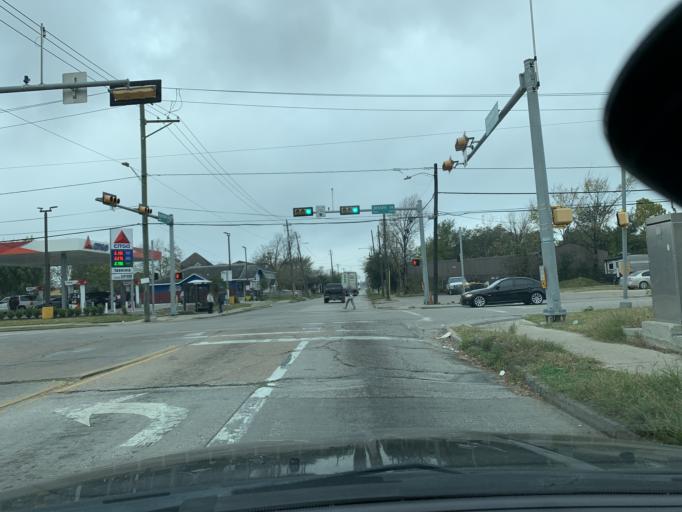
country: US
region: Texas
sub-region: Harris County
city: Houston
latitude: 29.7836
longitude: -95.3417
